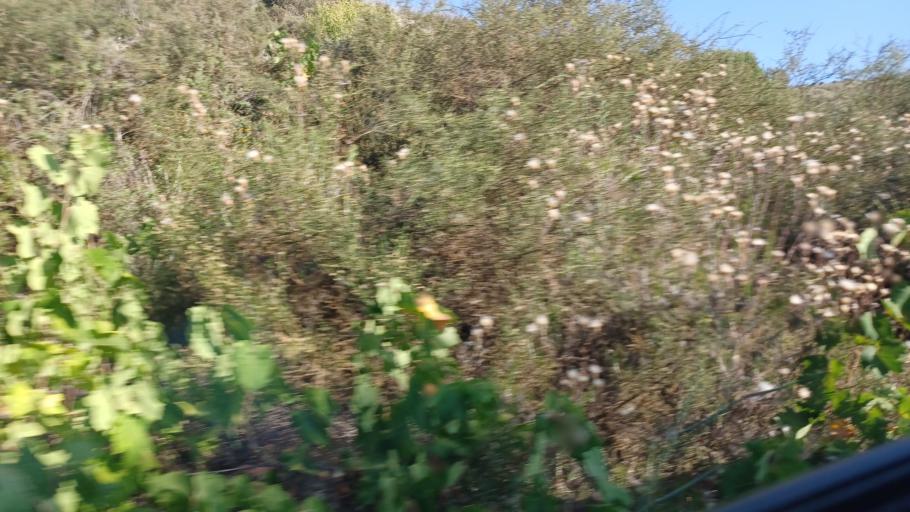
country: CY
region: Pafos
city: Tala
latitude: 34.8956
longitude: 32.4514
